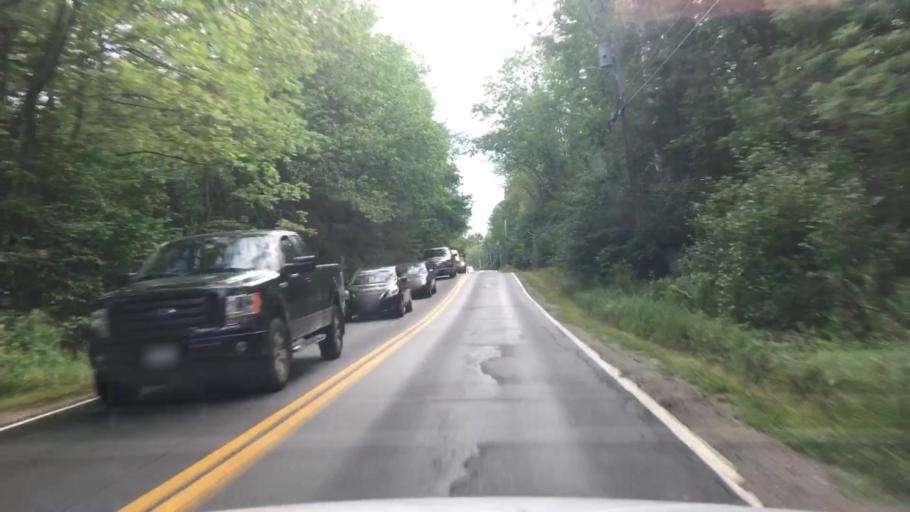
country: US
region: Maine
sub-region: Hancock County
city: Trenton
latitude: 44.4578
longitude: -68.4251
